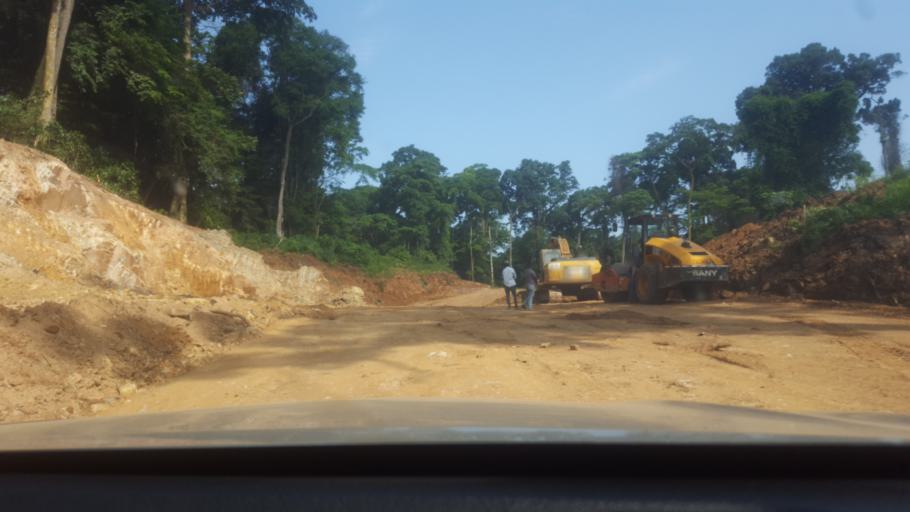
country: ET
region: Southern Nations, Nationalities, and People's Region
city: Tippi
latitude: 7.5387
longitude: 34.9799
